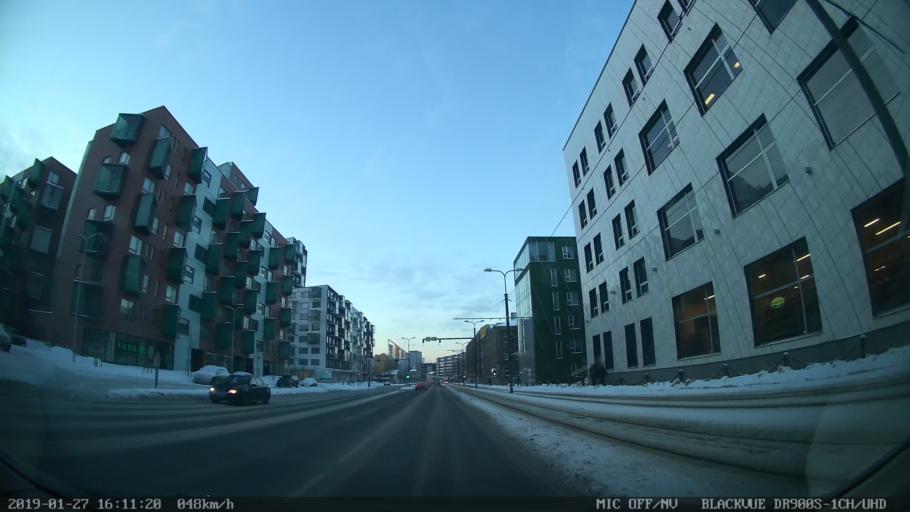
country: EE
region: Harju
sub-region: Tallinna linn
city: Tallinn
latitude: 59.4296
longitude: 24.7731
